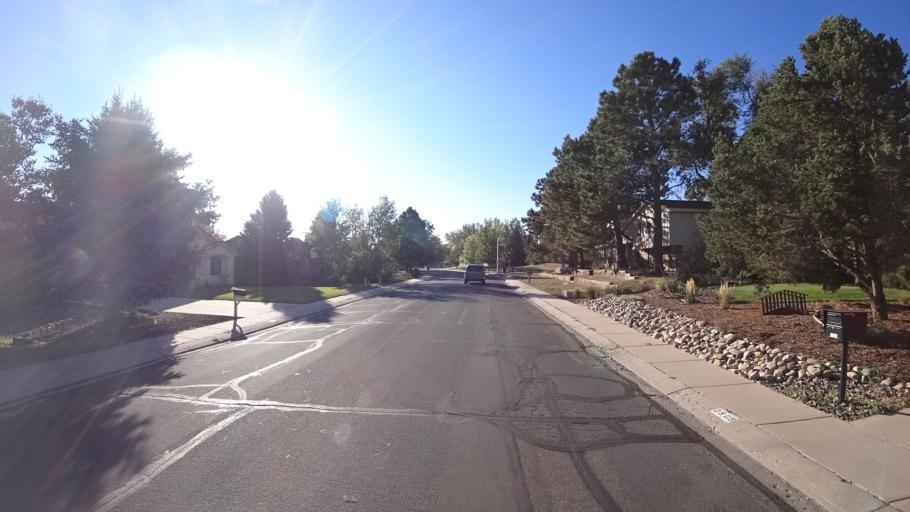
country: US
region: Colorado
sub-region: El Paso County
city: Cimarron Hills
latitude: 38.8873
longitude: -104.7643
